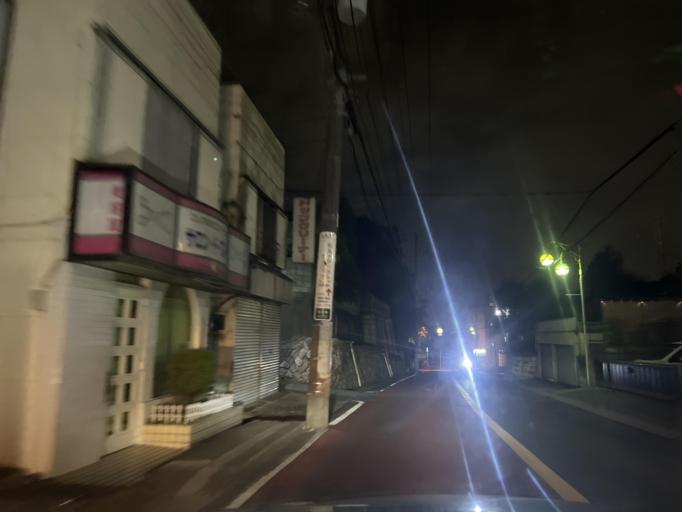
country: JP
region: Chiba
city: Matsudo
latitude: 35.7380
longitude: 139.9343
